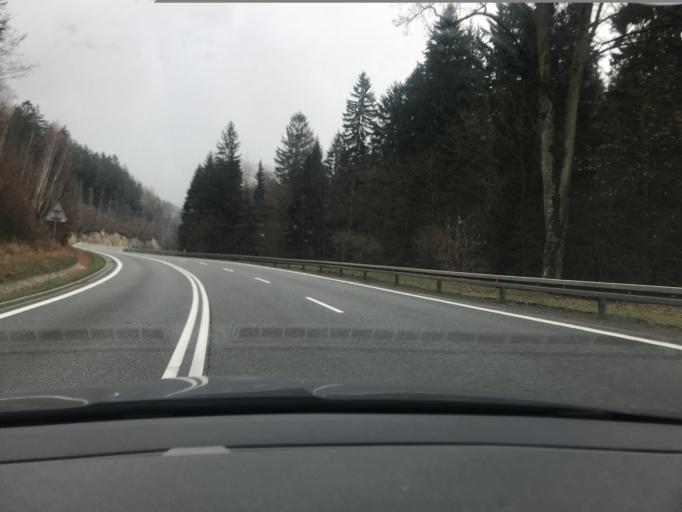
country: PL
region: Lower Silesian Voivodeship
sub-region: Powiat klodzki
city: Lewin Klodzki
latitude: 50.4030
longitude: 16.3355
